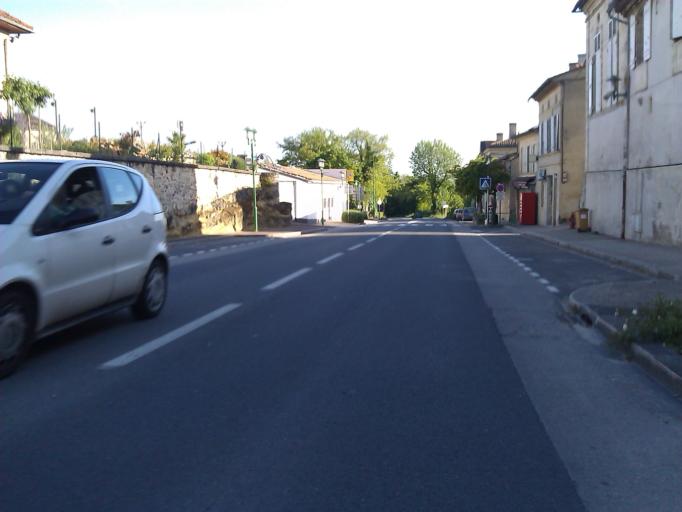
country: FR
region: Aquitaine
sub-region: Departement de la Gironde
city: Cubzac-les-Ponts
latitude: 44.9703
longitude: -0.4541
